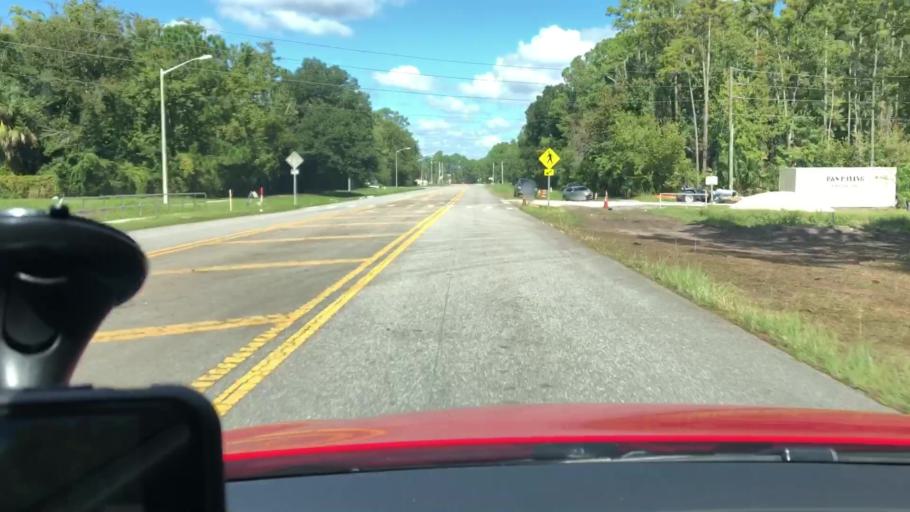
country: US
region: Florida
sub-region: Volusia County
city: Daytona Beach
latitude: 29.2076
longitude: -81.0675
